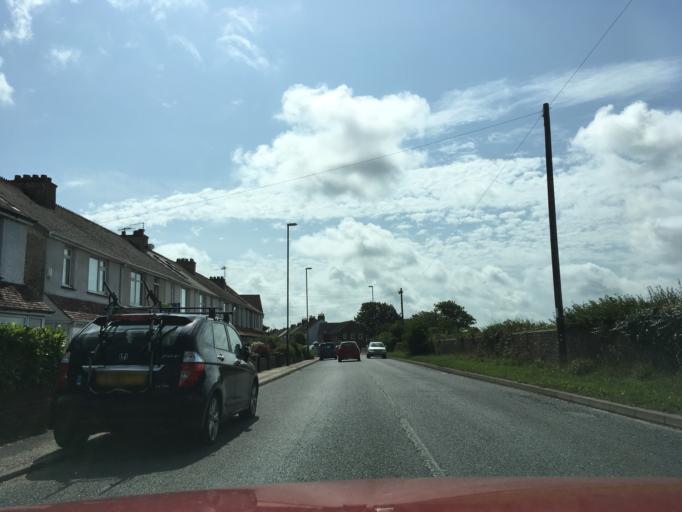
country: GB
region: England
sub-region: West Sussex
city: Shoreham-by-Sea
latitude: 50.8383
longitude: -0.2850
